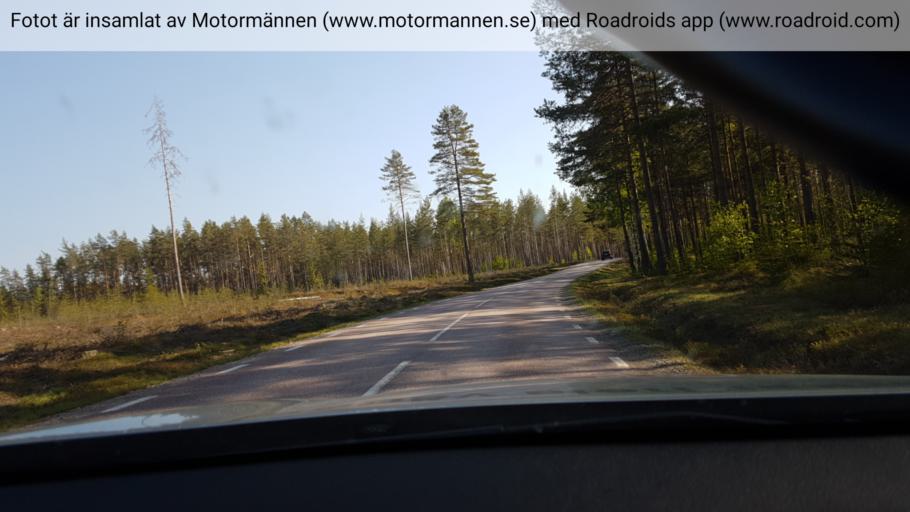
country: SE
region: Gaevleborg
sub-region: Sandvikens Kommun
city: Arsunda
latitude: 60.4912
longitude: 16.7233
